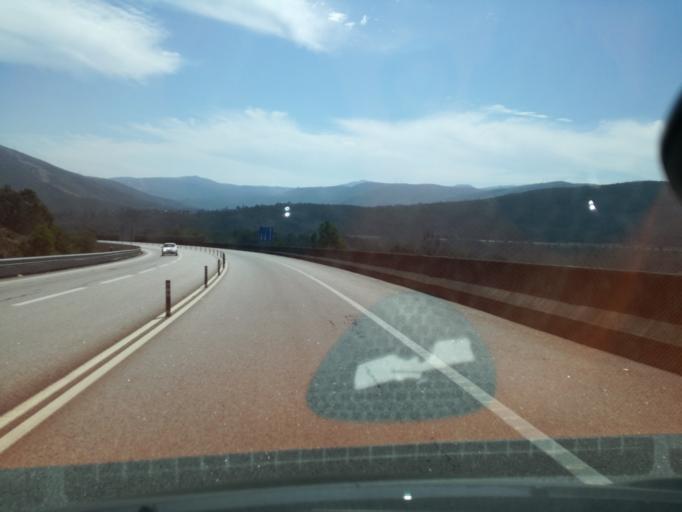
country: PT
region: Viana do Castelo
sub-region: Vila Nova de Cerveira
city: Vila Nova de Cerveira
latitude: 41.8969
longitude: -8.7855
